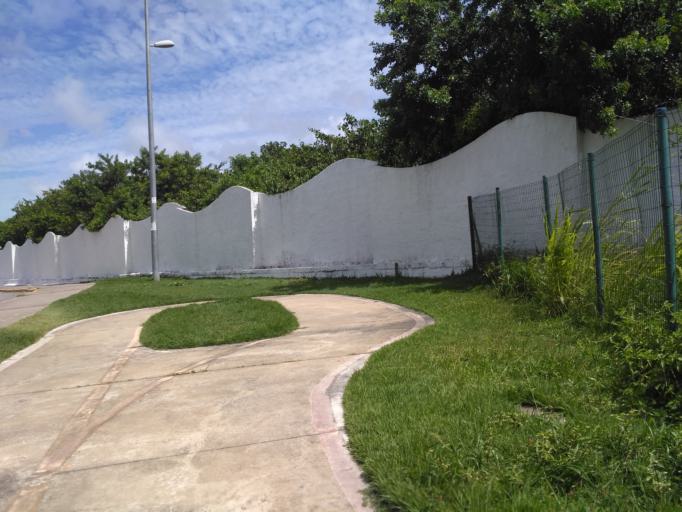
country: BR
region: Pernambuco
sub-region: Recife
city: Recife
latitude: -8.0860
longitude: -34.8969
